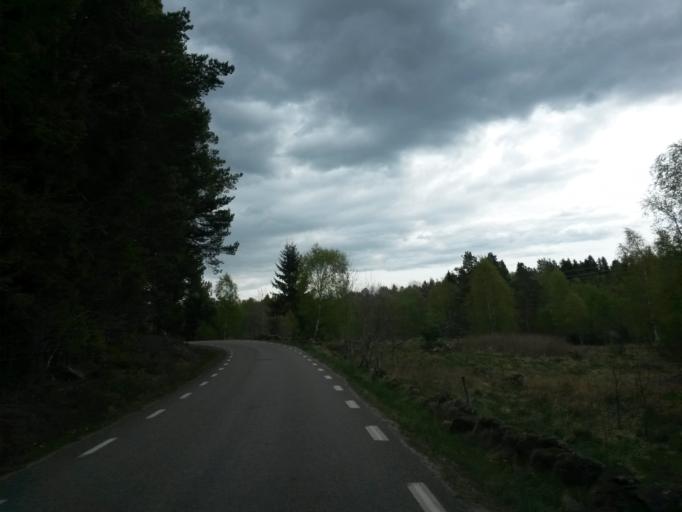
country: SE
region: Vaestra Goetaland
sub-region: Herrljunga Kommun
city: Herrljunga
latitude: 58.1400
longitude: 13.0394
